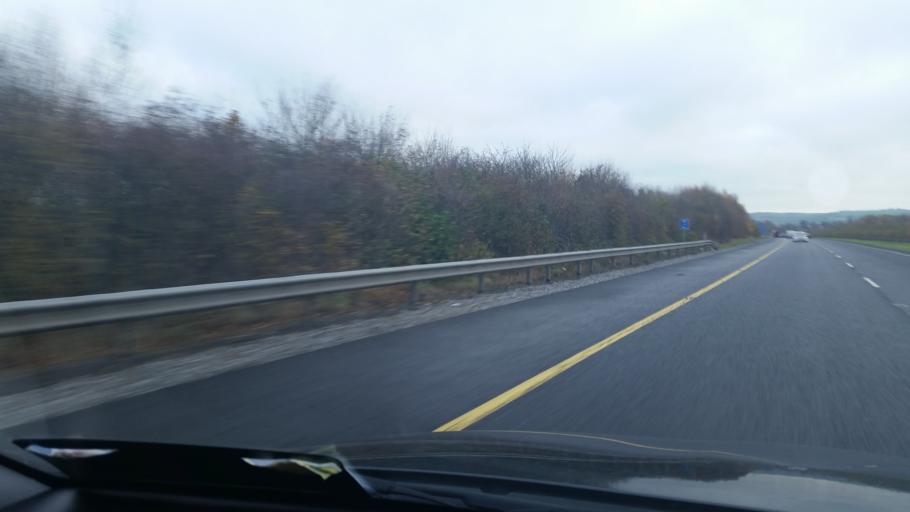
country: IE
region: Leinster
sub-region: Lu
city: Drogheda
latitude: 53.6772
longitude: -6.3566
